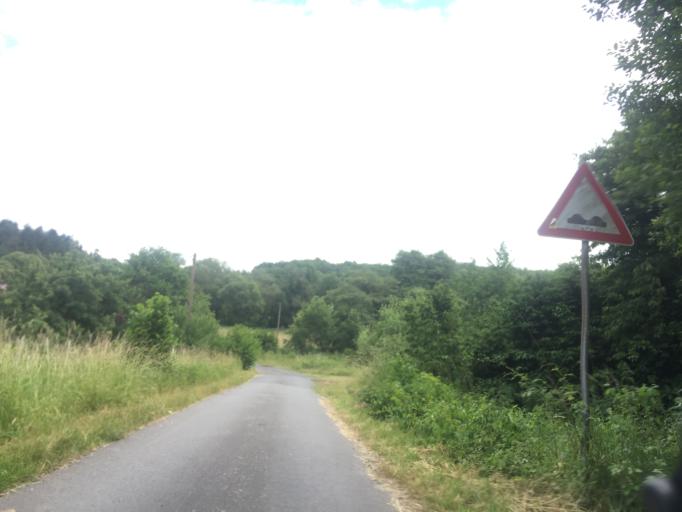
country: DE
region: Rheinland-Pfalz
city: Girod
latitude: 50.4482
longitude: 7.9286
